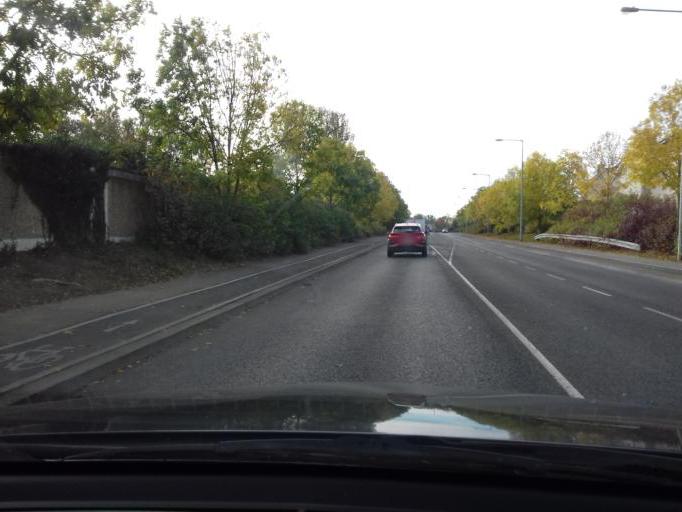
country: IE
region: Leinster
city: Hartstown
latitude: 53.3898
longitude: -6.4135
